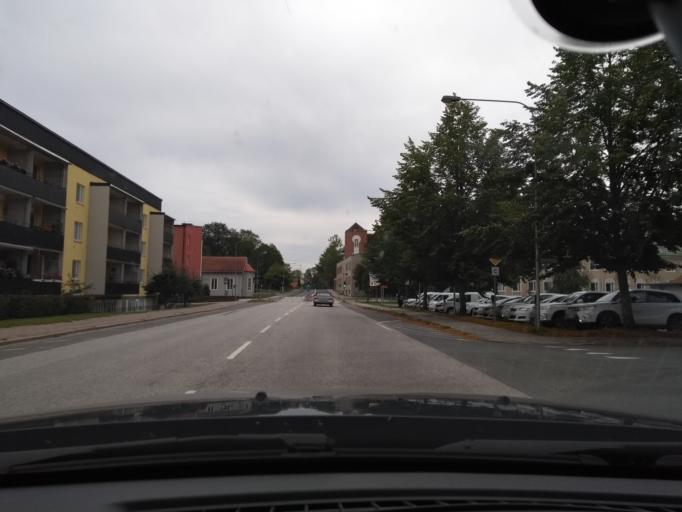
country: SE
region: Joenkoeping
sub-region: Eksjo Kommun
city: Eksjoe
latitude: 57.6683
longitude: 14.9738
